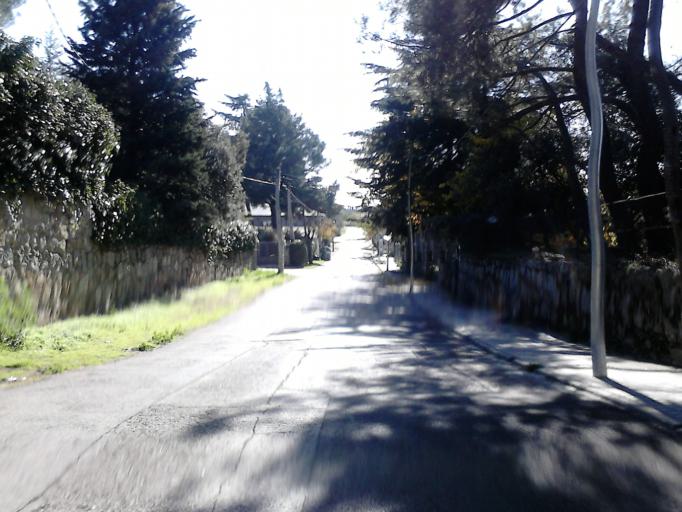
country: ES
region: Madrid
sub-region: Provincia de Madrid
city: Torrelodones
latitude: 40.5863
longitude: -3.9649
